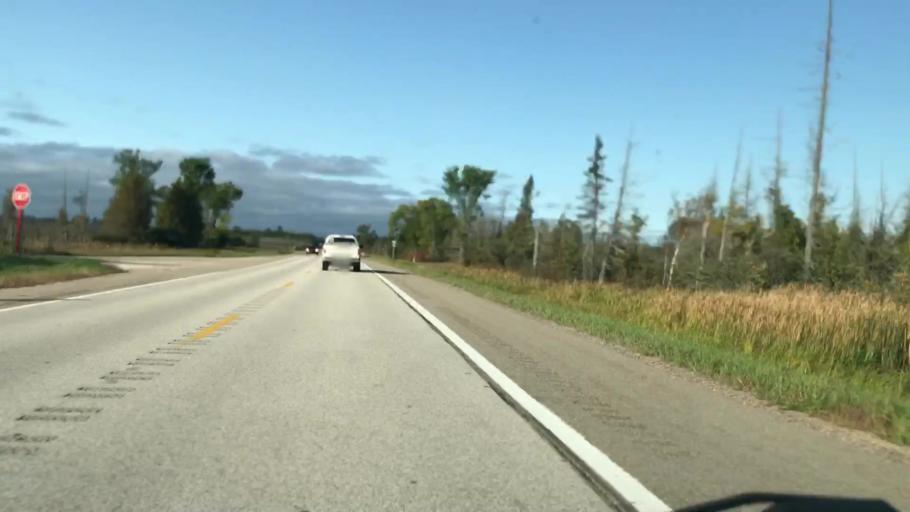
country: US
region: Michigan
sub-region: Luce County
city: Newberry
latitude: 46.3183
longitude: -85.1929
